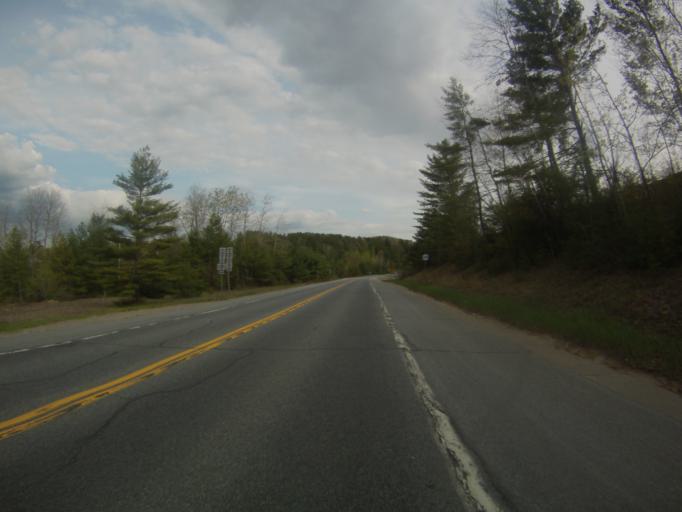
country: US
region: New York
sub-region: Warren County
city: Warrensburg
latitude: 43.6964
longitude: -73.9884
